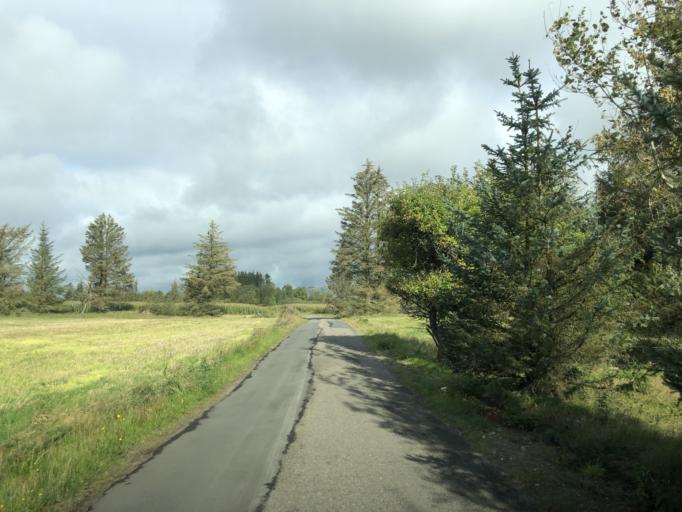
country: DK
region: Central Jutland
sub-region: Holstebro Kommune
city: Ulfborg
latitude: 56.2930
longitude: 8.4545
